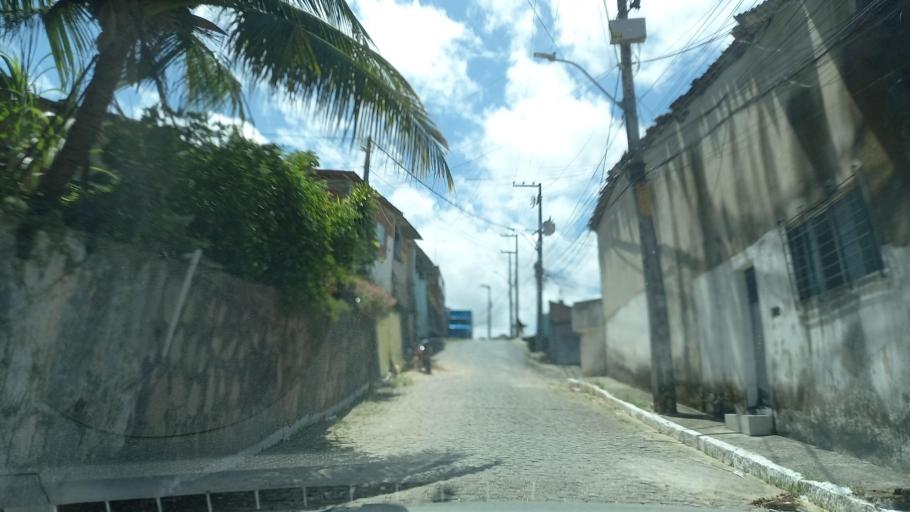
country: BR
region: Pernambuco
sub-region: Jaboatao Dos Guararapes
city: Jaboatao dos Guararapes
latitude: -8.1333
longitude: -34.9559
